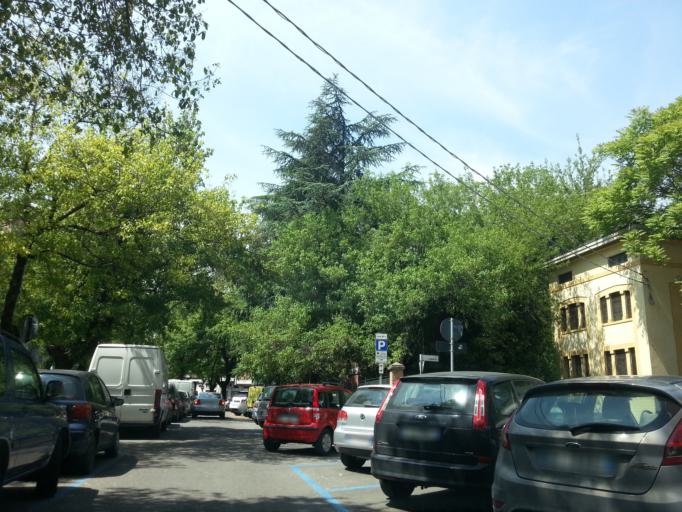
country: IT
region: Emilia-Romagna
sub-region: Provincia di Reggio Emilia
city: Reggio nell'Emilia
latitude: 44.6926
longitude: 10.6317
